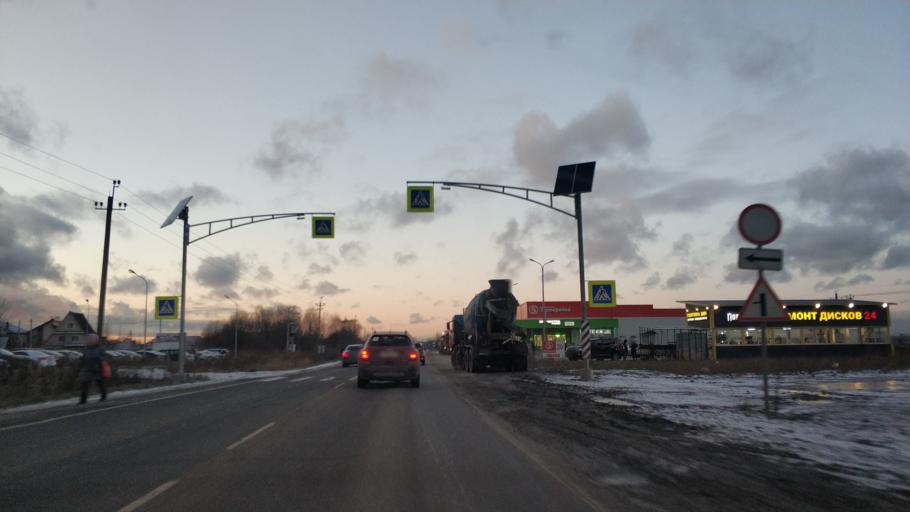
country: RU
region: St.-Petersburg
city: Pontonnyy
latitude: 59.8013
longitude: 30.6340
